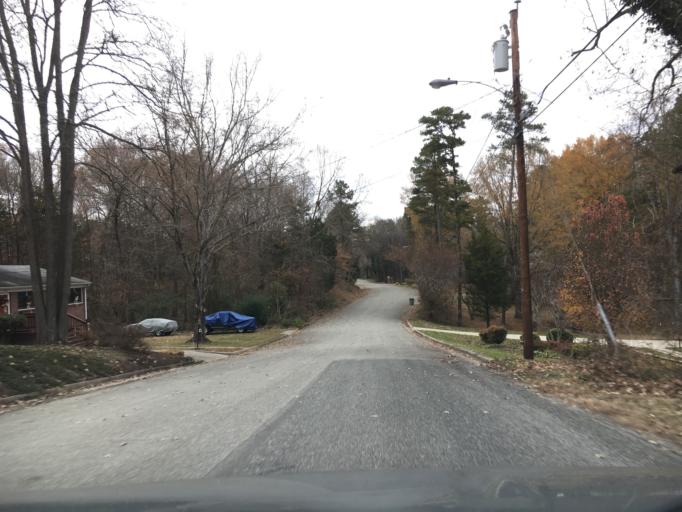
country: US
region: Virginia
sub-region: Halifax County
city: South Boston
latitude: 36.7067
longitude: -78.8922
